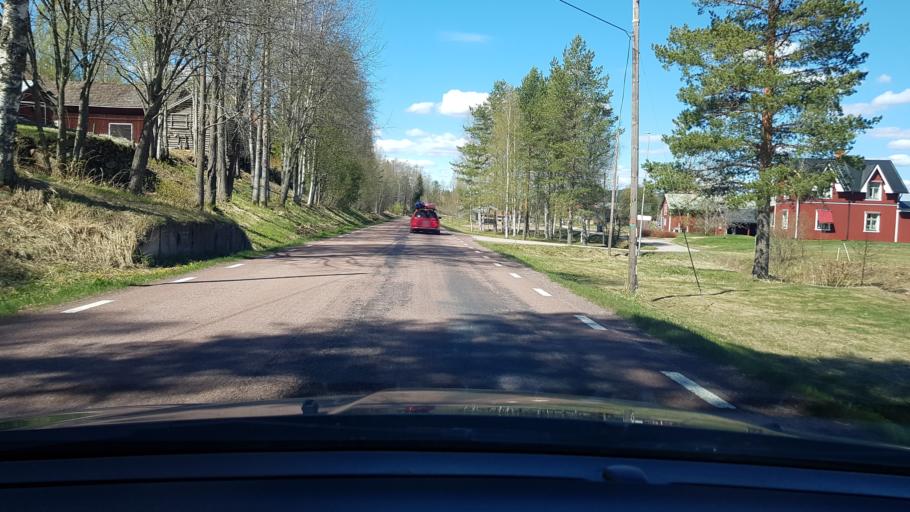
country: SE
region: Dalarna
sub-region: Alvdalens Kommun
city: AElvdalen
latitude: 61.1171
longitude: 14.1647
